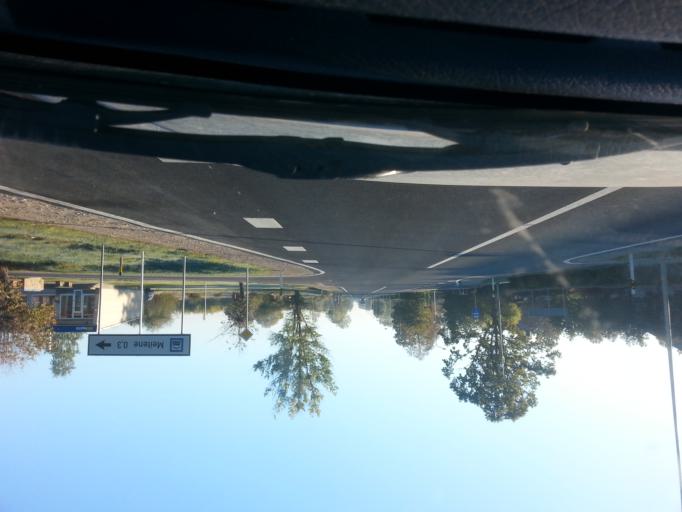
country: LT
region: Siauliu apskritis
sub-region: Joniskis
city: Joniskis
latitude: 56.4086
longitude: 23.6820
